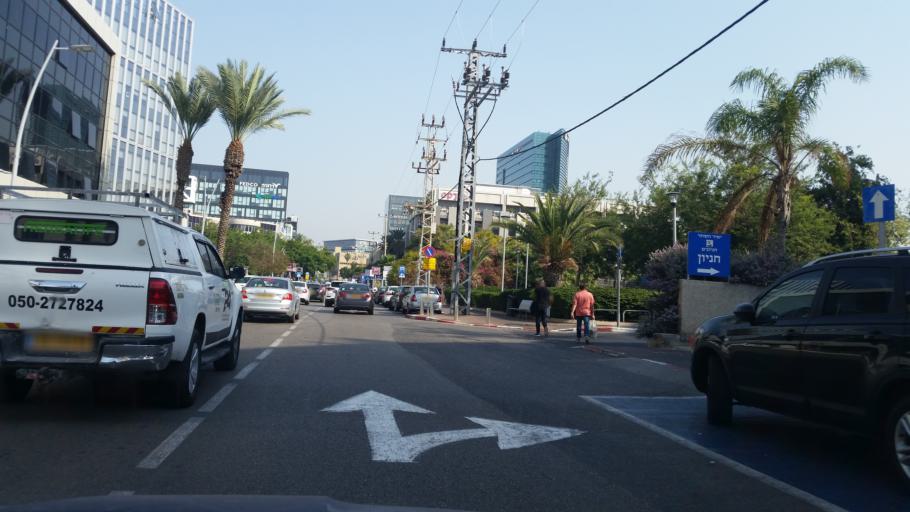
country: IL
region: Tel Aviv
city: Herzliya Pituah
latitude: 32.1623
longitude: 34.8097
